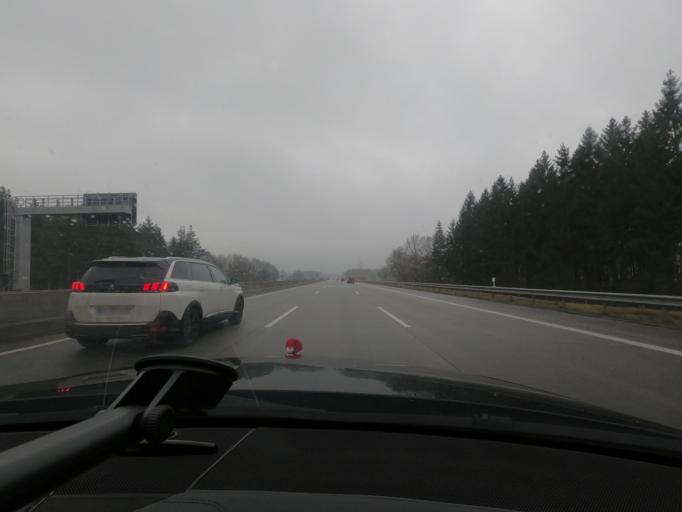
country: DE
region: Schleswig-Holstein
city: Schmalfeld
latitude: 53.8947
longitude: 9.9401
